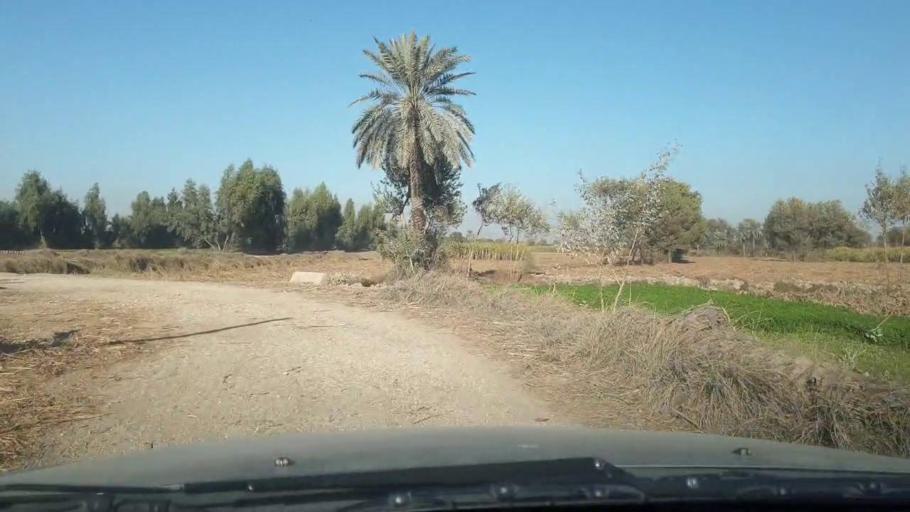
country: PK
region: Sindh
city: Adilpur
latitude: 27.9555
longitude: 69.1993
